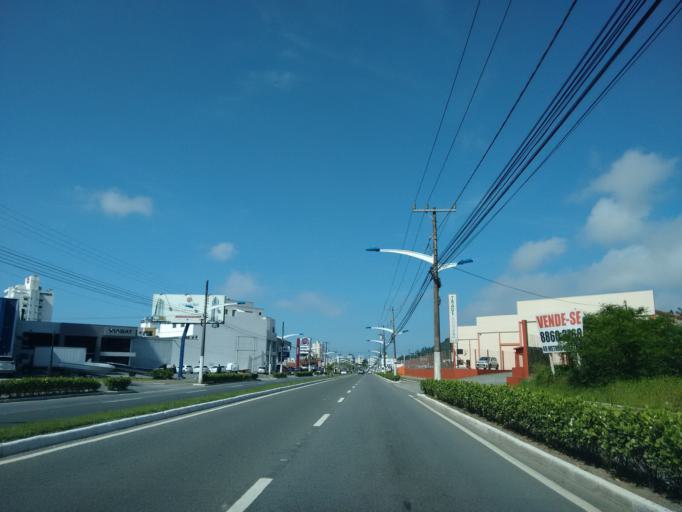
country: BR
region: Santa Catarina
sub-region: Itajai
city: Itajai
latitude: -26.9272
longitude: -48.6814
